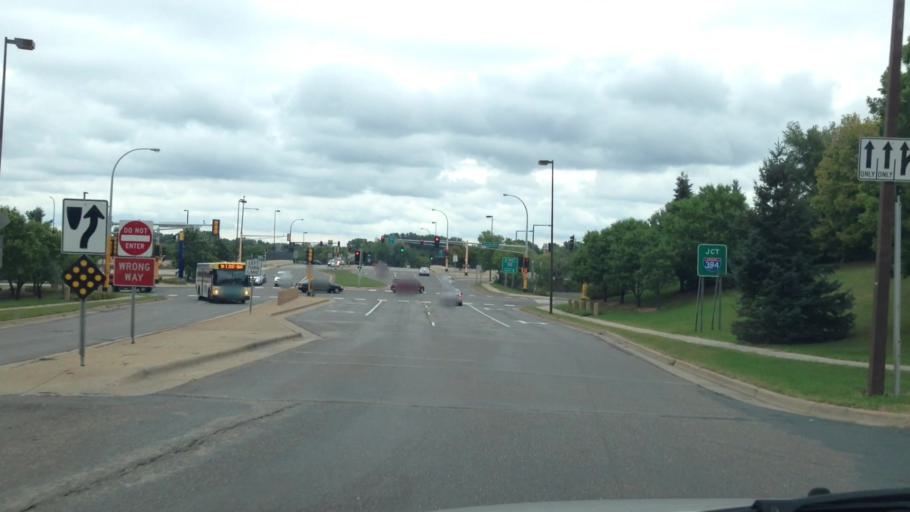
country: US
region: Minnesota
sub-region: Hennepin County
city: Saint Louis Park
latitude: 44.9693
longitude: -93.3707
